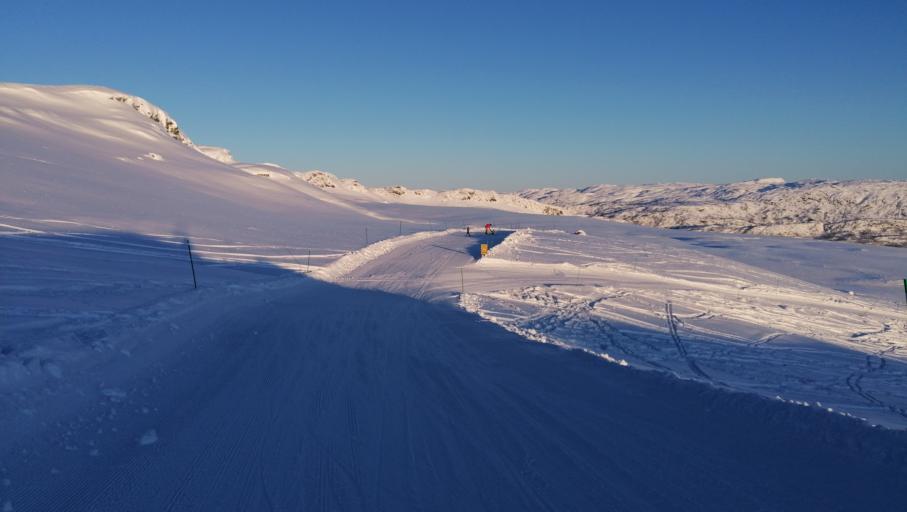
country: NO
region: Aust-Agder
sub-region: Bykle
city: Hovden
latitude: 59.5824
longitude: 7.3316
